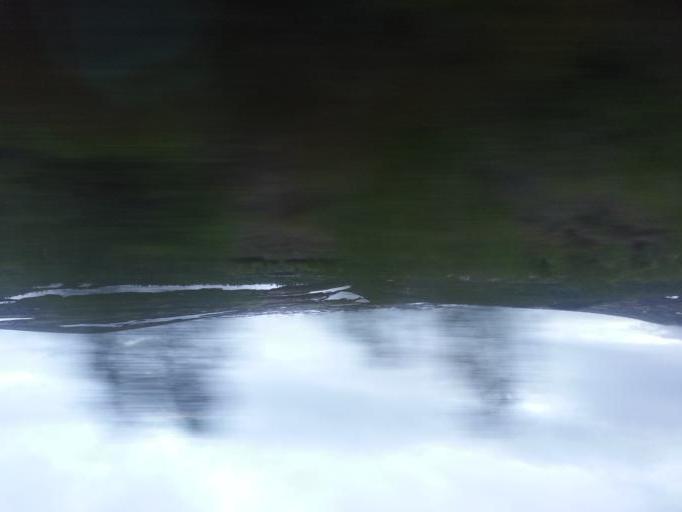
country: NO
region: Oppland
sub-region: Dovre
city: Dovre
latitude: 62.1160
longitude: 9.2721
